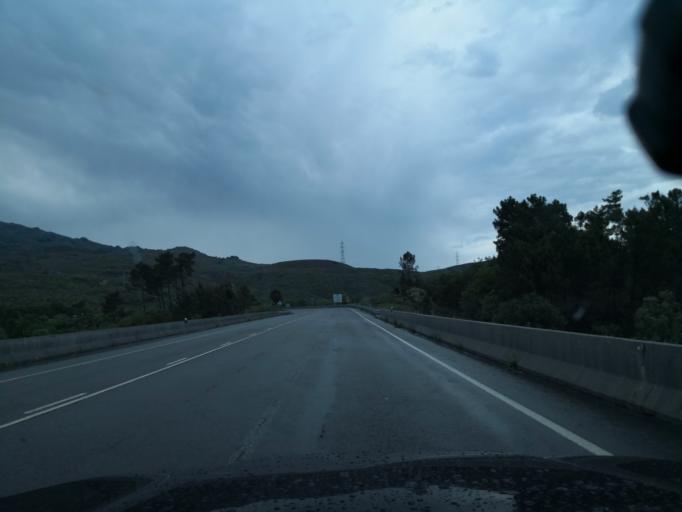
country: PT
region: Vila Real
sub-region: Vila Real
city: Vila Real
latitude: 41.3751
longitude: -7.7148
